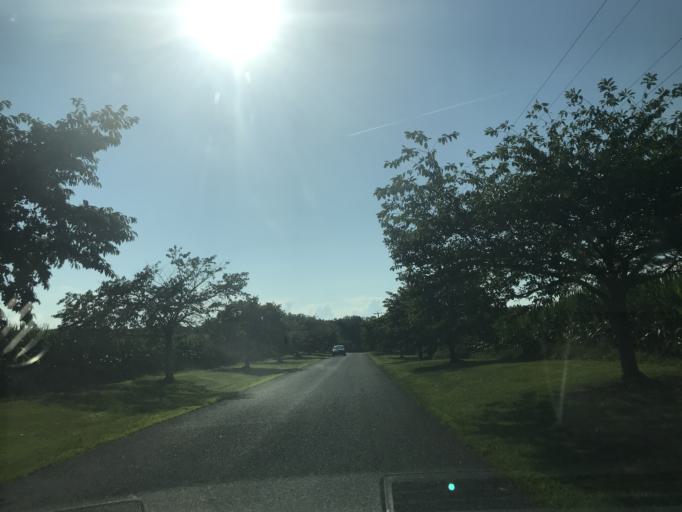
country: US
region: Maryland
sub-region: Harford County
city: Havre de Grace
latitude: 39.5217
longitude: -76.1176
